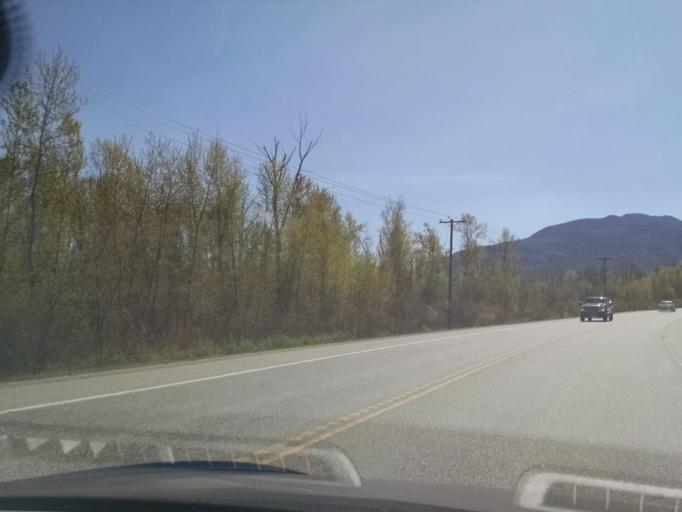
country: CA
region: British Columbia
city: Salmon Arm
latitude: 50.7315
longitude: -119.3160
